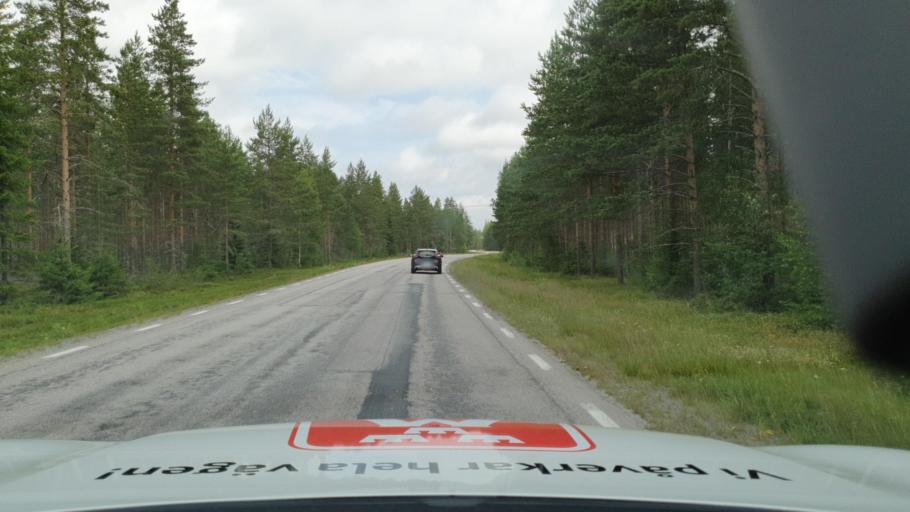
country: SE
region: Vaesterbotten
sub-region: Umea Kommun
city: Roback
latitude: 63.8599
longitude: 20.1445
